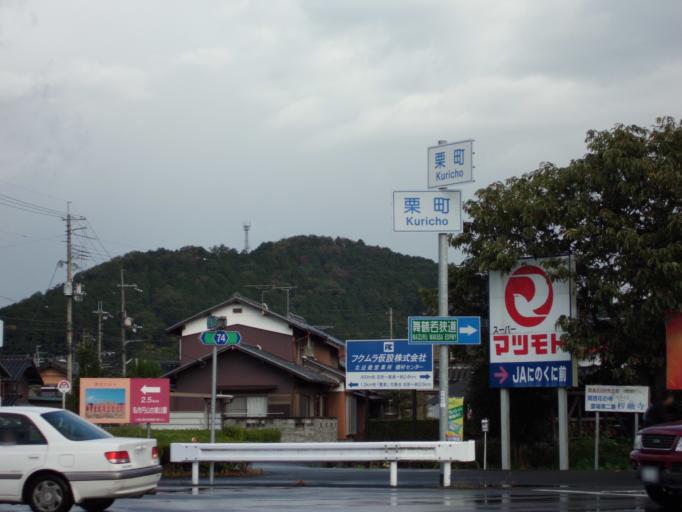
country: JP
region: Kyoto
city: Ayabe
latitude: 35.3117
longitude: 135.2201
